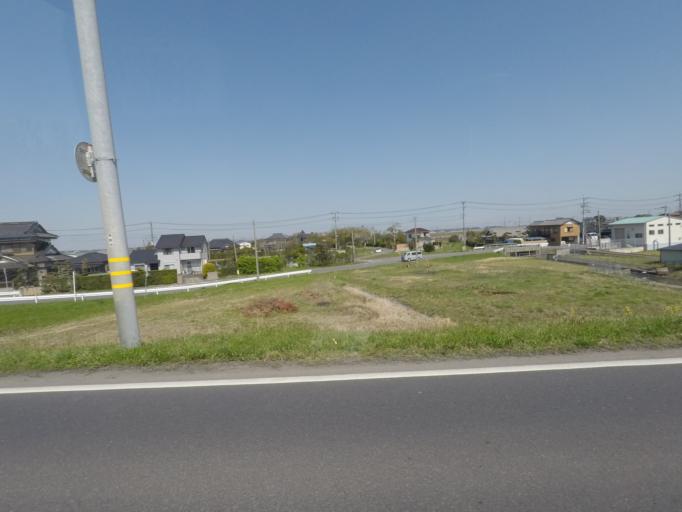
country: JP
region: Chiba
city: Katori-shi
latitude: 35.9160
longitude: 140.4401
